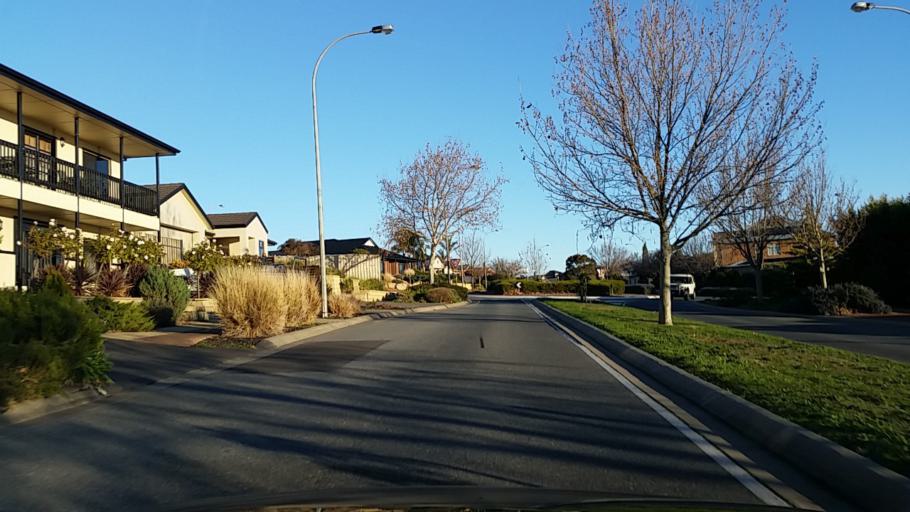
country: AU
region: South Australia
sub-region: Onkaparinga
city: Moana
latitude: -35.2072
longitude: 138.4880
